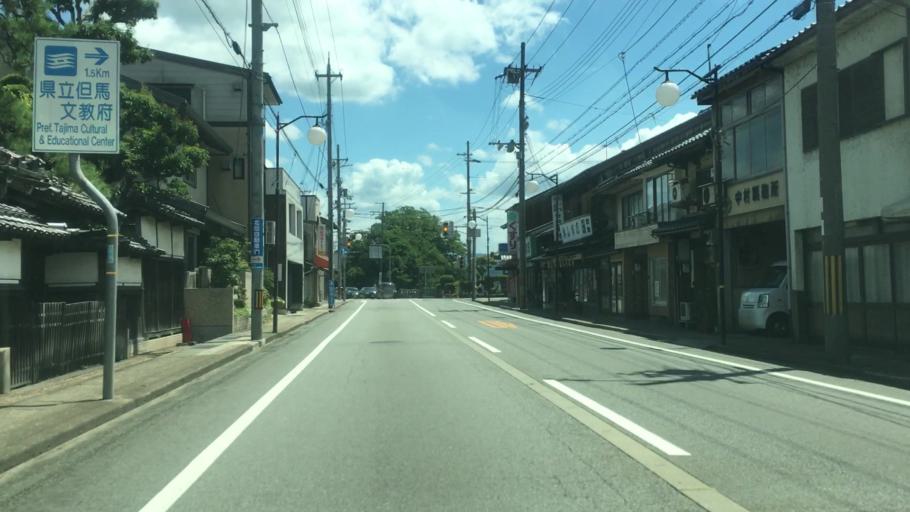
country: JP
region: Hyogo
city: Toyooka
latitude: 35.5362
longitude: 134.8253
